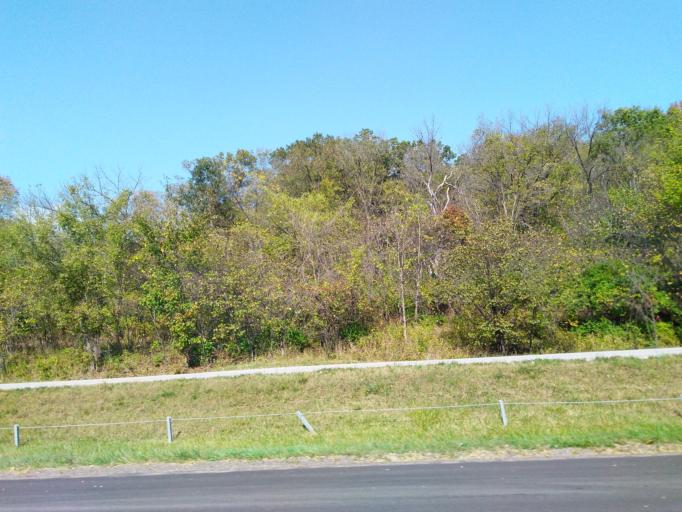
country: US
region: Missouri
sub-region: Saint Louis County
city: Valley Park
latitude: 38.5350
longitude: -90.5180
